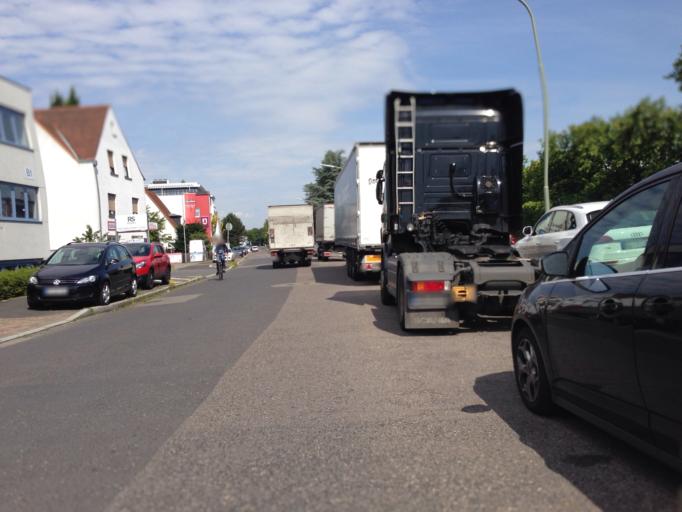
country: DE
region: Hesse
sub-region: Regierungsbezirk Darmstadt
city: Hanau am Main
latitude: 50.1194
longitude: 8.9250
